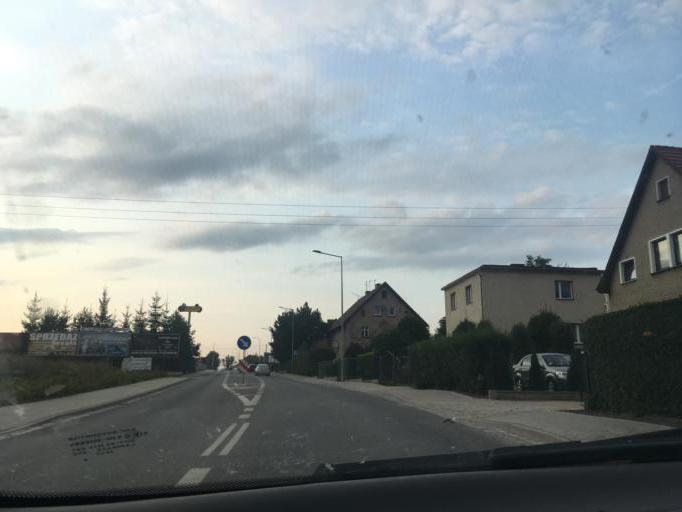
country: PL
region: Lower Silesian Voivodeship
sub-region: Powiat klodzki
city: Bozkow
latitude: 50.5477
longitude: 16.5509
